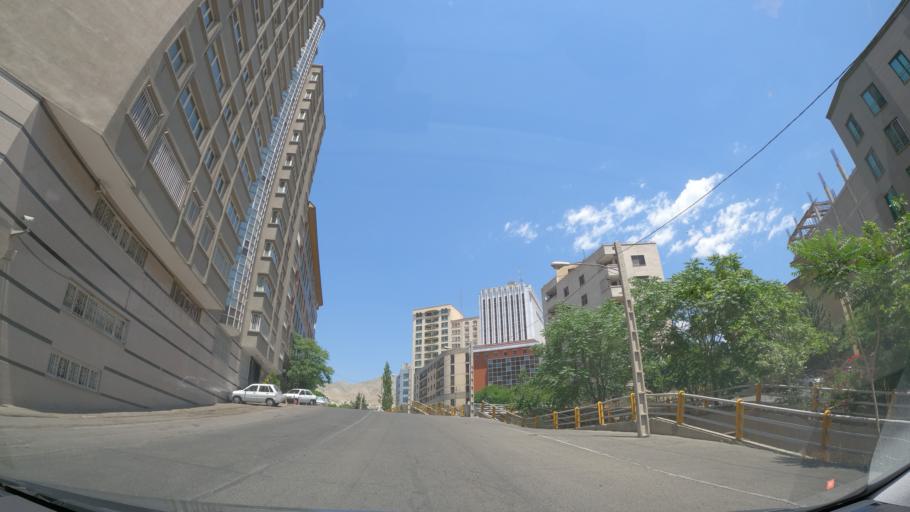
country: IR
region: Tehran
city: Tajrish
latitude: 35.7808
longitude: 51.3862
